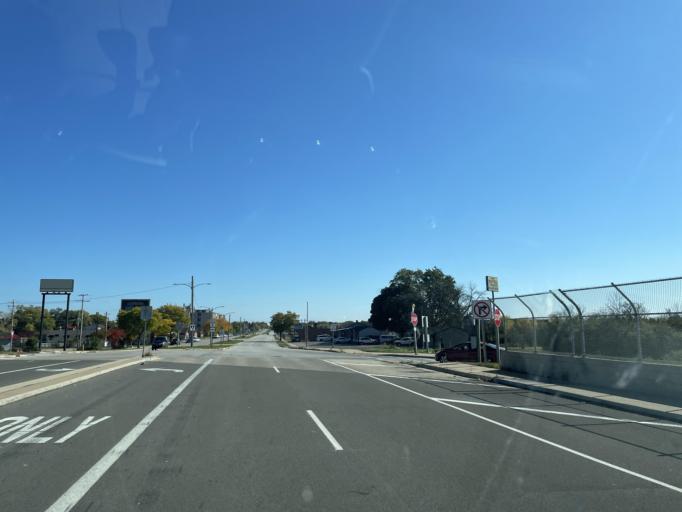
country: US
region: Wisconsin
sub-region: Waukesha County
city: Butler
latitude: 43.1196
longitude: -88.0351
